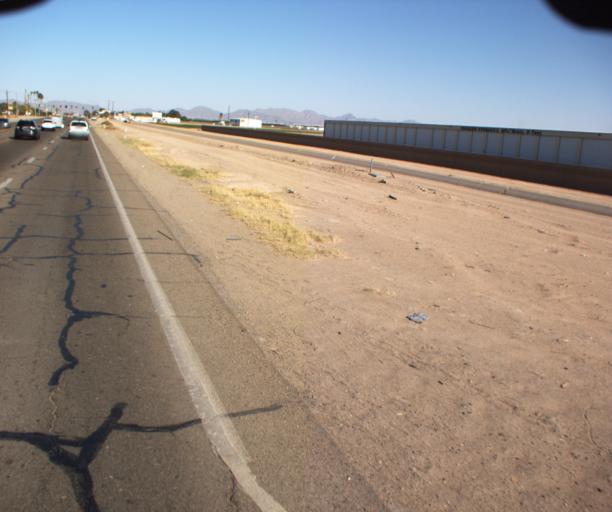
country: US
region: Arizona
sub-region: Yuma County
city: Yuma
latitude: 32.6697
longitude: -114.5682
